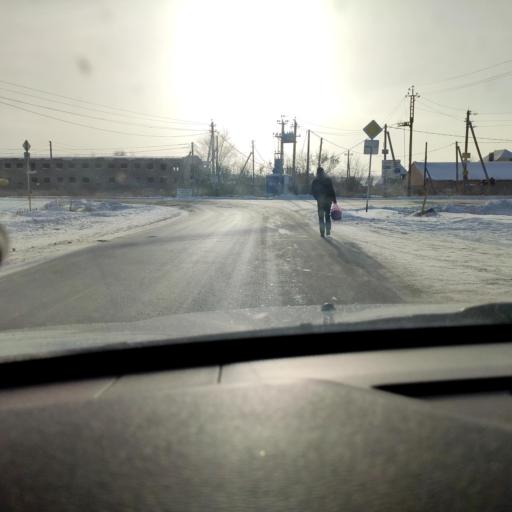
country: RU
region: Samara
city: Smyshlyayevka
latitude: 53.1607
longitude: 50.3824
